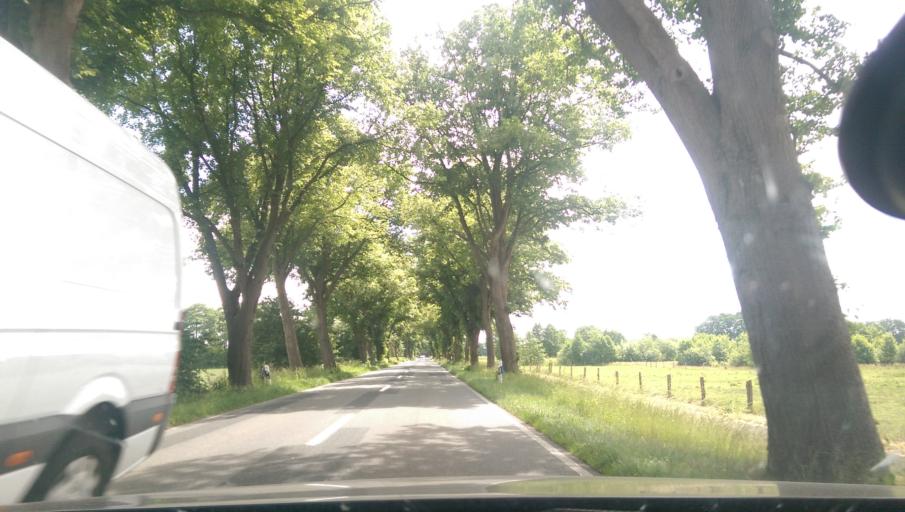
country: DE
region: Lower Saxony
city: Oyten
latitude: 53.1063
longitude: 9.0549
